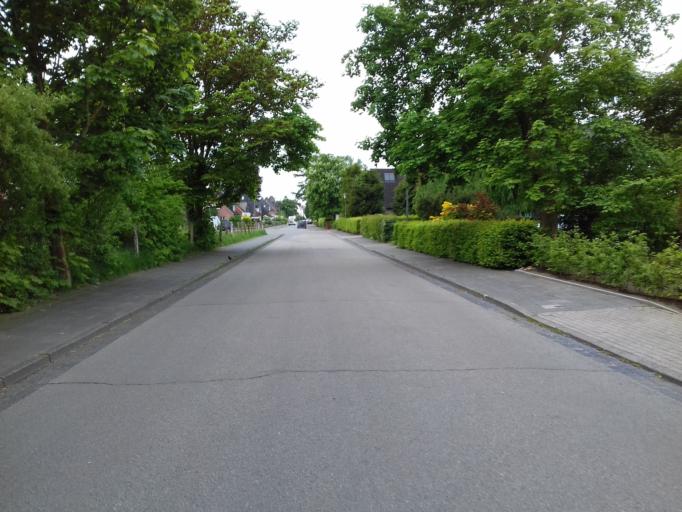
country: DE
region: Schleswig-Holstein
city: Neumunster
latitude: 54.0799
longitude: 10.0003
